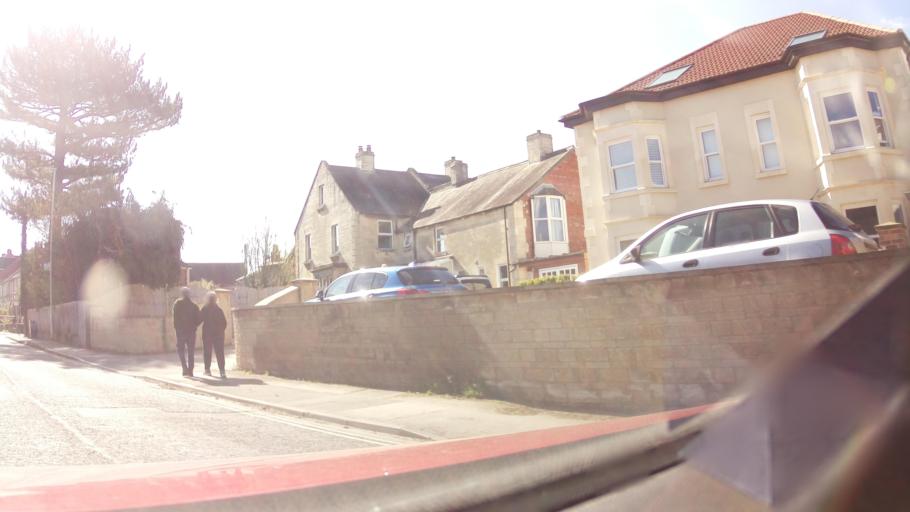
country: GB
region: England
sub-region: Wiltshire
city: Trowbridge
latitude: 51.3198
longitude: -2.2174
